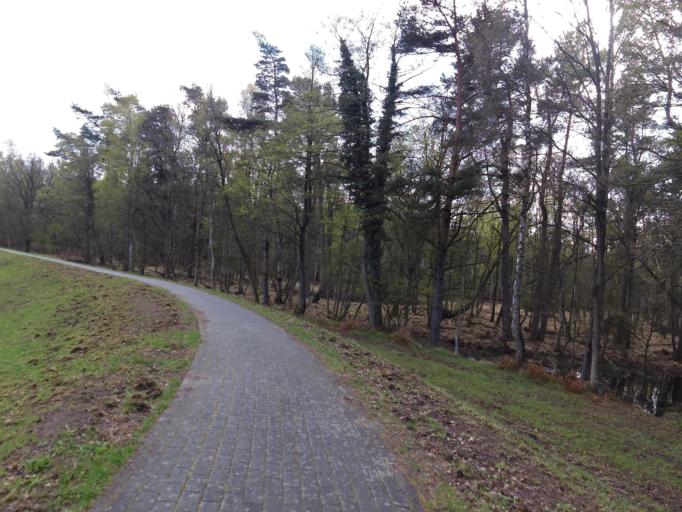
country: DE
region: Mecklenburg-Vorpommern
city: Zingst
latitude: 54.4325
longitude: 12.6633
